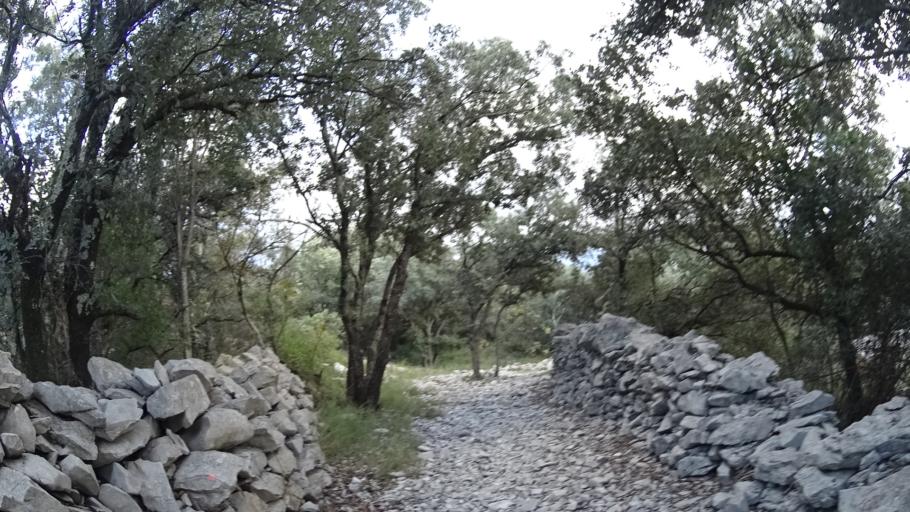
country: FR
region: Languedoc-Roussillon
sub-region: Departement de l'Herault
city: Claret
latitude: 43.8642
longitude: 3.9156
